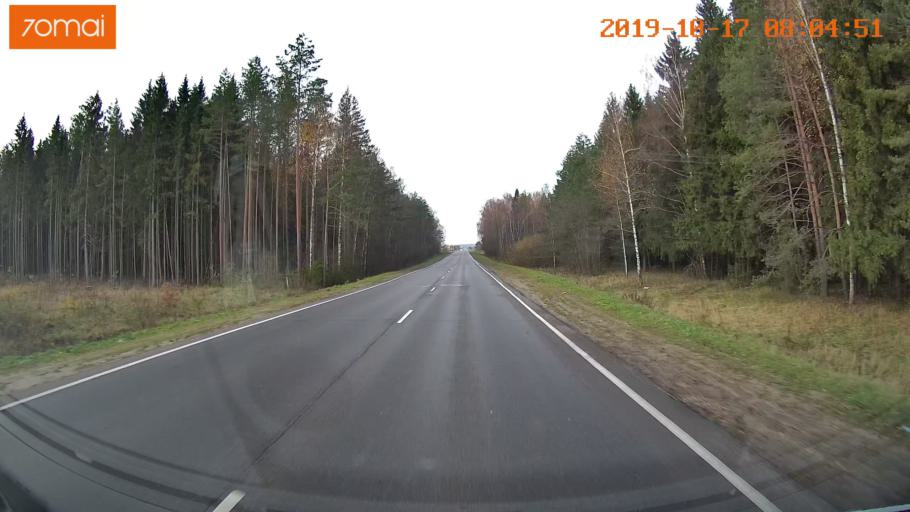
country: RU
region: Vladimir
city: Belaya Rechka
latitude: 56.3409
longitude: 39.4271
